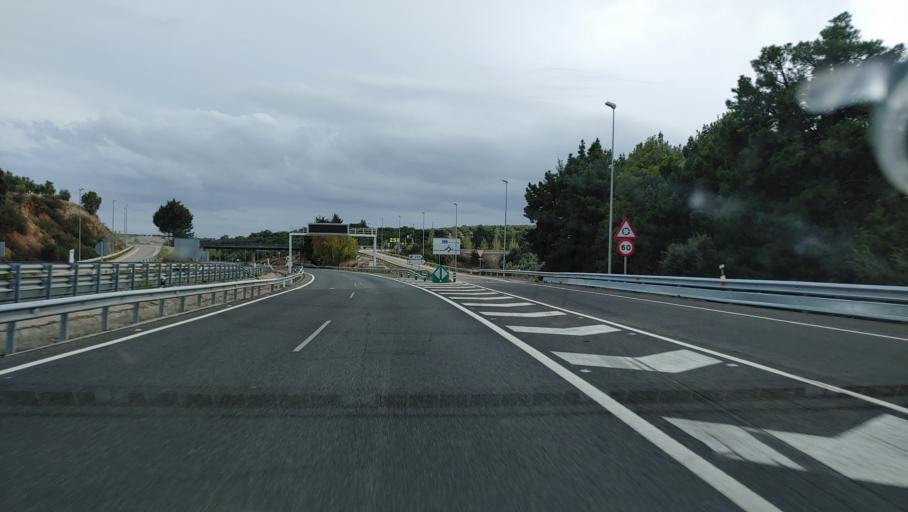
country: ES
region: Andalusia
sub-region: Provincia de Jaen
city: Santa Elena
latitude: 38.3404
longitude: -3.5458
